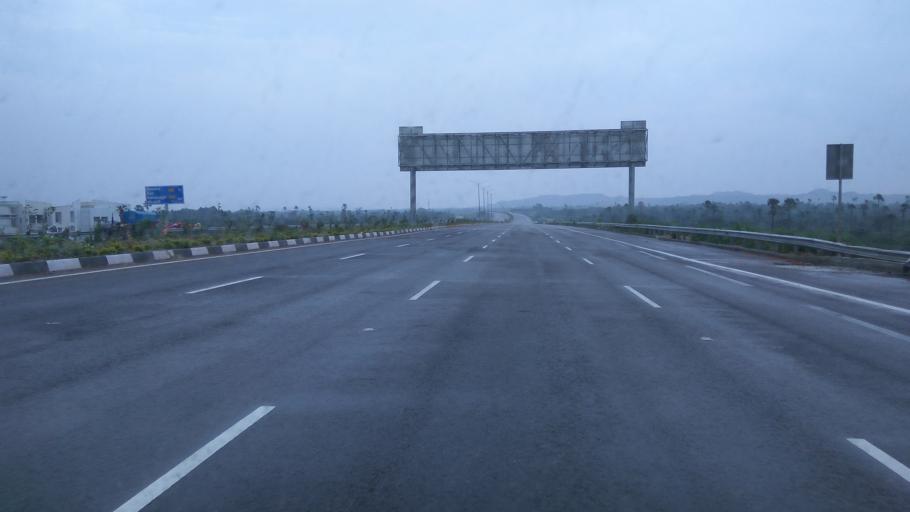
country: IN
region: Telangana
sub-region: Rangareddi
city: Ghatkesar
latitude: 17.4536
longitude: 78.6688
